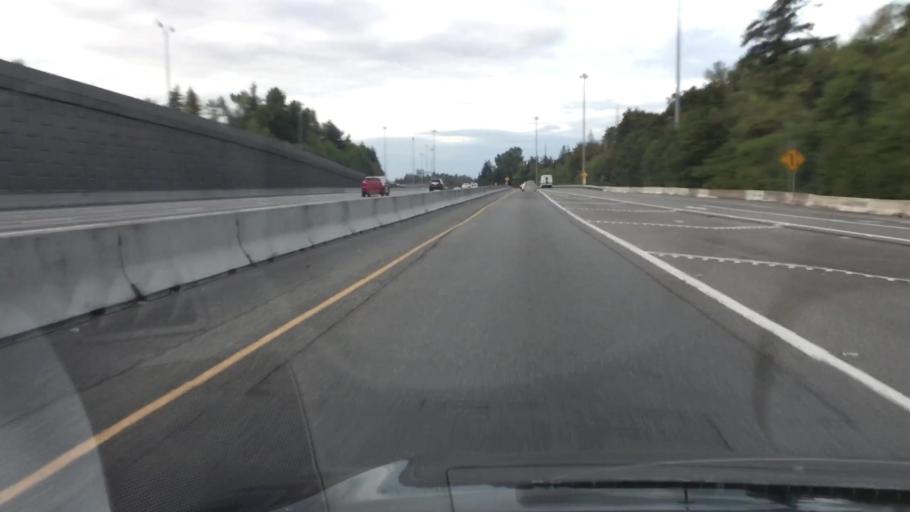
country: US
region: Washington
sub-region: King County
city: Federal Way
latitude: 47.3175
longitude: -122.2960
